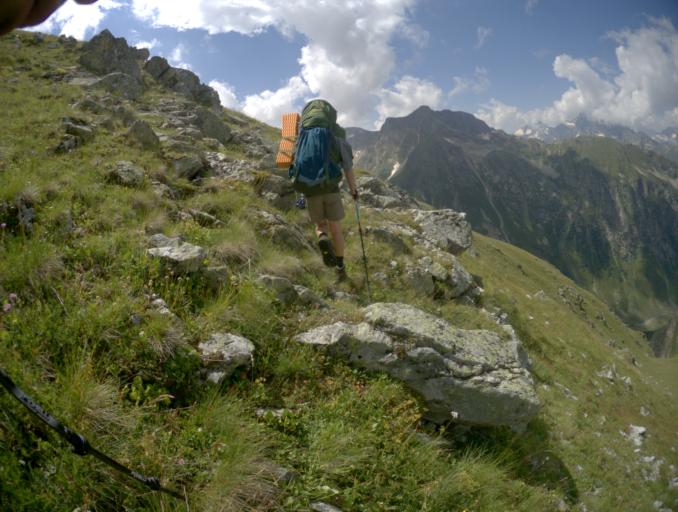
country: RU
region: Karachayevo-Cherkesiya
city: Uchkulan
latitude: 43.2974
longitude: 42.0687
